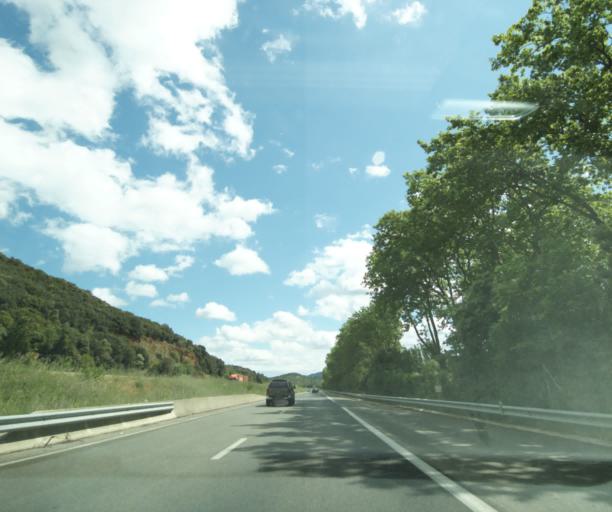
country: FR
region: Languedoc-Roussillon
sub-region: Departement de l'Herault
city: Lodeve
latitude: 43.7076
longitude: 3.3267
